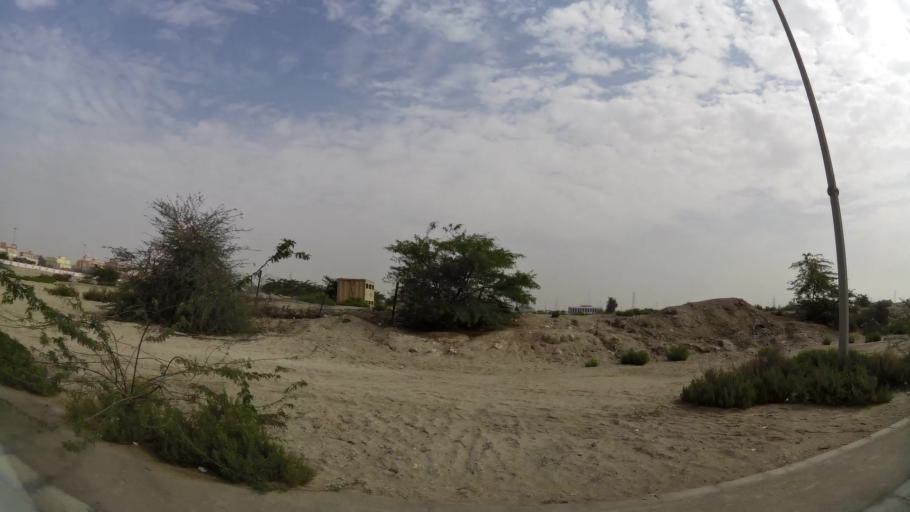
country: AE
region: Abu Dhabi
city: Abu Dhabi
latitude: 24.2890
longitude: 54.6570
